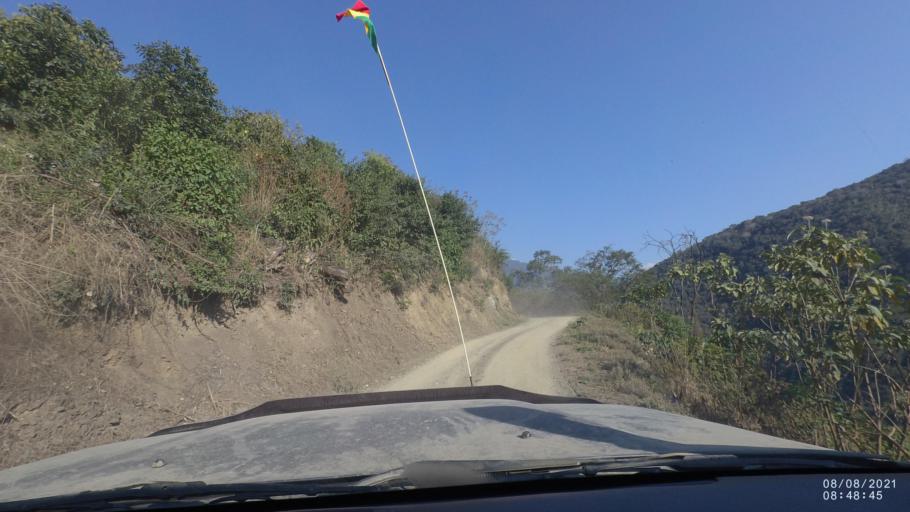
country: BO
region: La Paz
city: Quime
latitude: -16.5312
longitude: -66.7555
